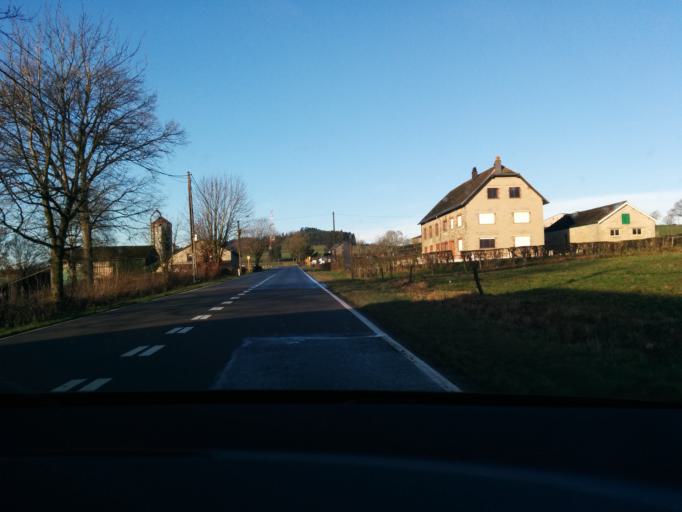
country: BE
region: Wallonia
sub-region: Province de Liege
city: Lierneux
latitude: 50.2615
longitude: 5.8387
